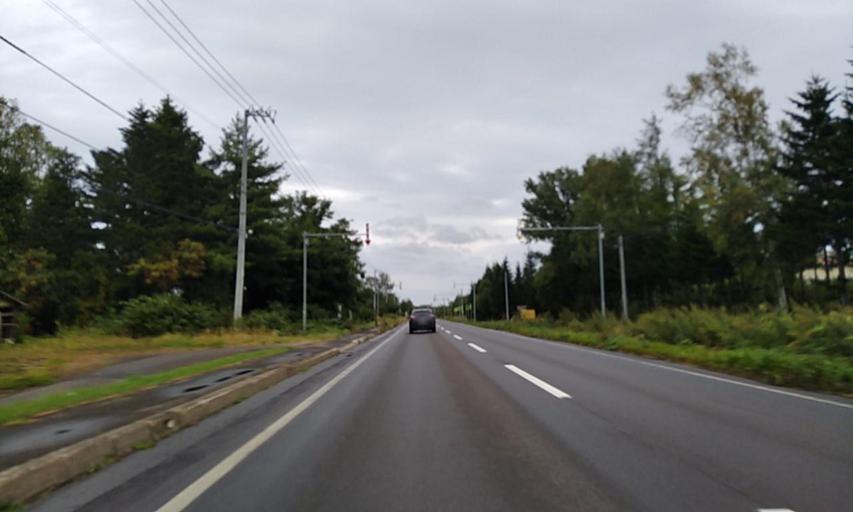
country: JP
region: Hokkaido
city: Kitami
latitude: 44.0846
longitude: 143.9488
